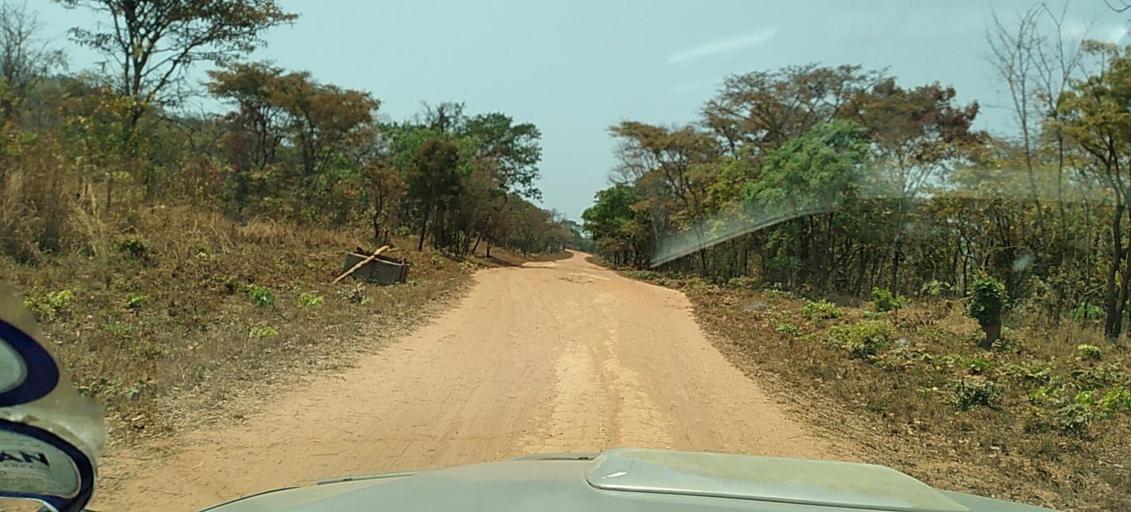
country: ZM
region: North-Western
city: Kasempa
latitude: -13.5508
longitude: 26.0223
